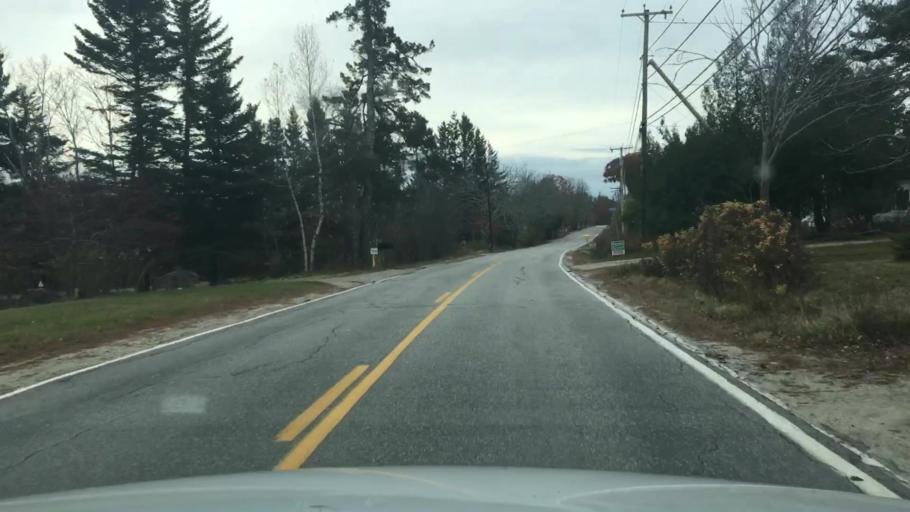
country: US
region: Maine
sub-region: Hancock County
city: Sedgwick
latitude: 44.3617
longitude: -68.5505
